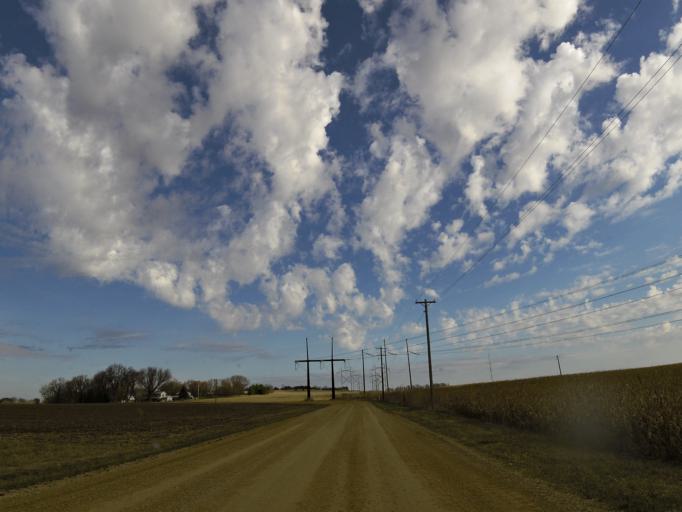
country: US
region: Minnesota
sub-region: Dakota County
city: Hastings
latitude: 44.7605
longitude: -92.8326
